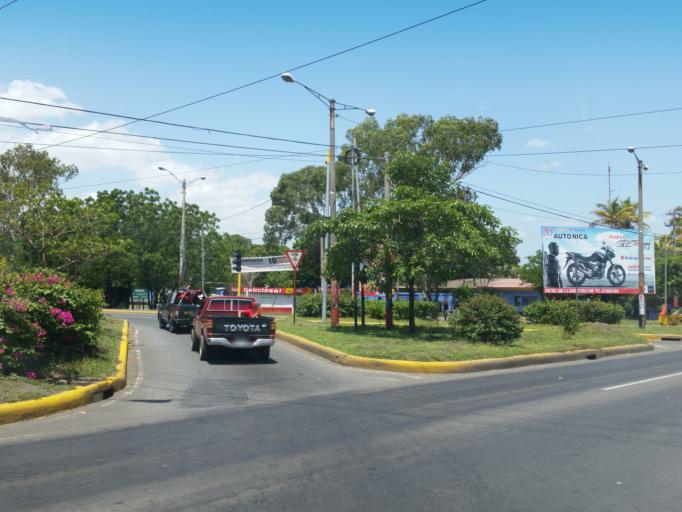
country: NI
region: Managua
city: Managua
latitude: 12.1479
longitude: -86.1950
